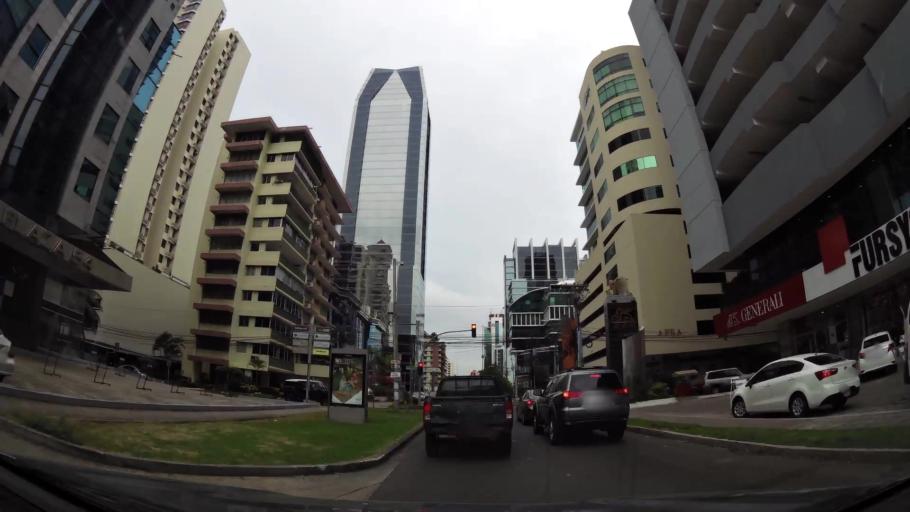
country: PA
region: Panama
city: Panama
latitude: 8.9852
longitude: -79.5219
